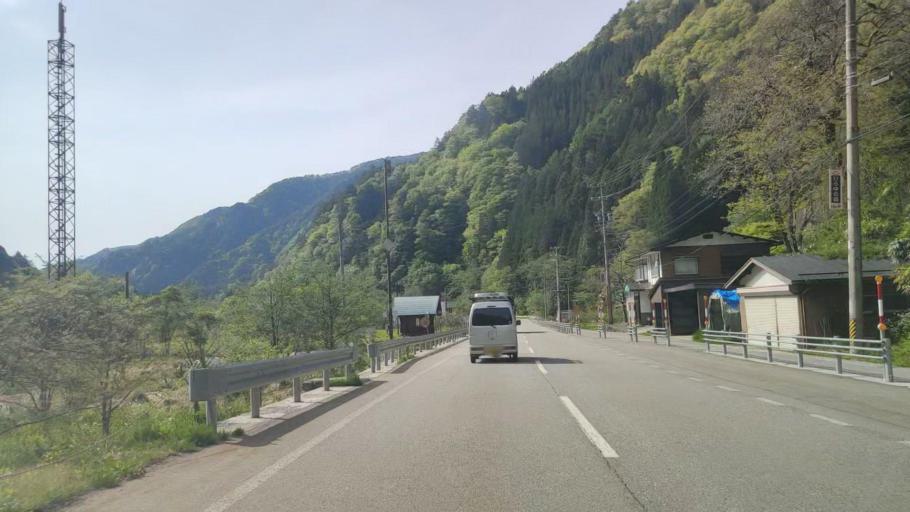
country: JP
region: Gifu
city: Takayama
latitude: 36.2529
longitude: 137.4777
